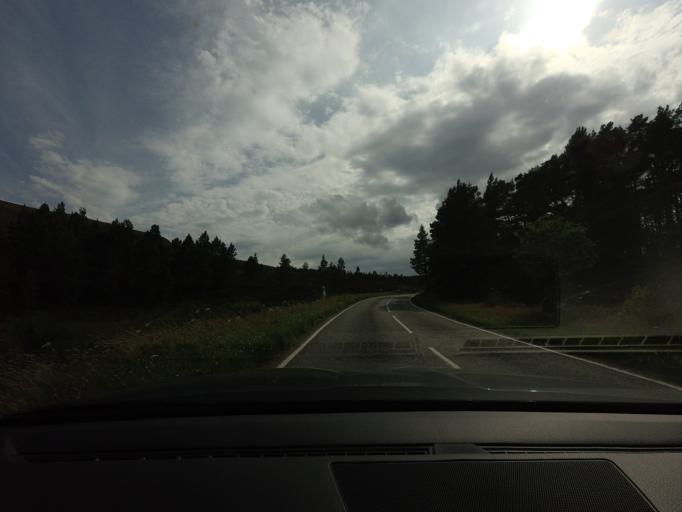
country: GB
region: Scotland
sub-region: Highland
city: Alness
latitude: 57.8388
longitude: -4.2687
